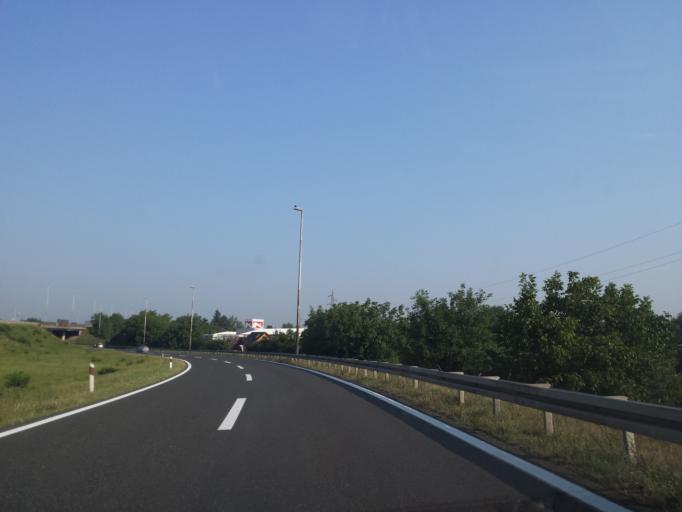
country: HR
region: Grad Zagreb
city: Zadvorsko
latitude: 45.7558
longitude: 15.9039
